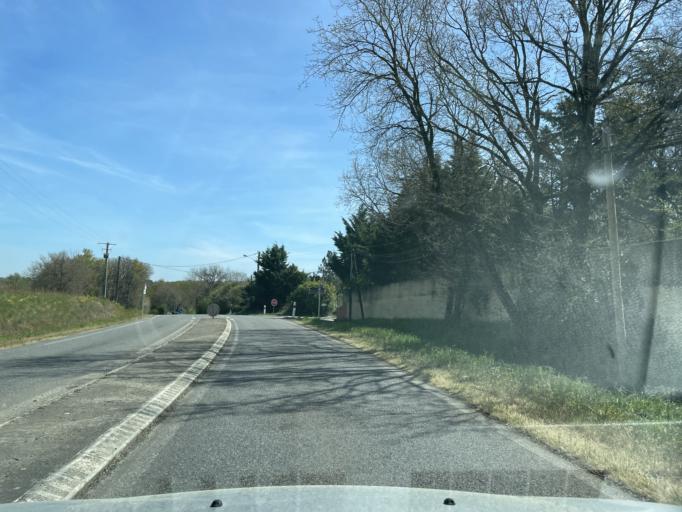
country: FR
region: Midi-Pyrenees
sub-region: Departement de la Haute-Garonne
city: Brax
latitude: 43.6191
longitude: 1.2520
